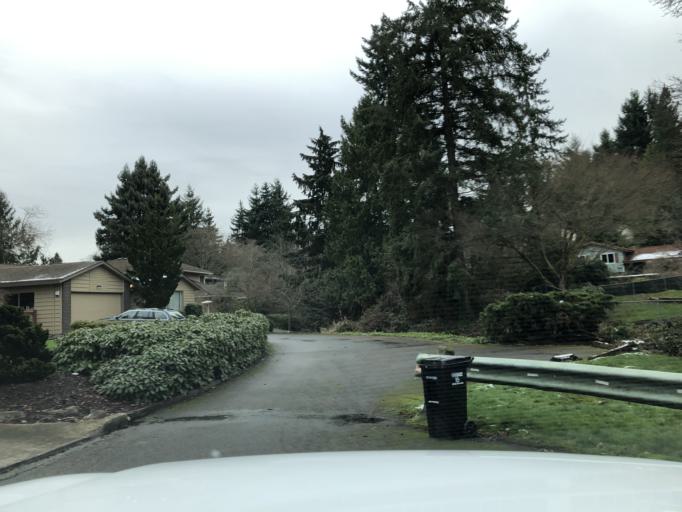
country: US
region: Washington
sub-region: King County
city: Inglewood-Finn Hill
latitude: 47.7007
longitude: -122.2814
